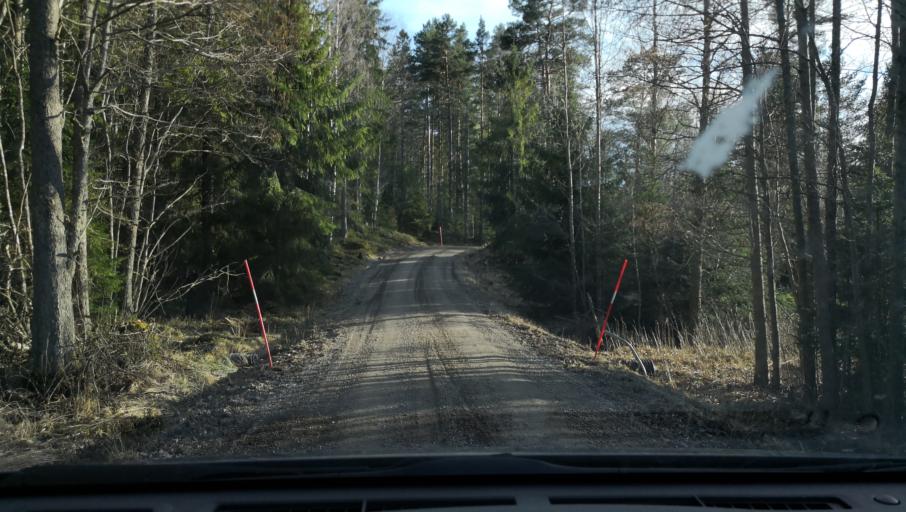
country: SE
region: Vaestmanland
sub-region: Arboga Kommun
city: Arboga
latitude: 59.4372
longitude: 15.7526
